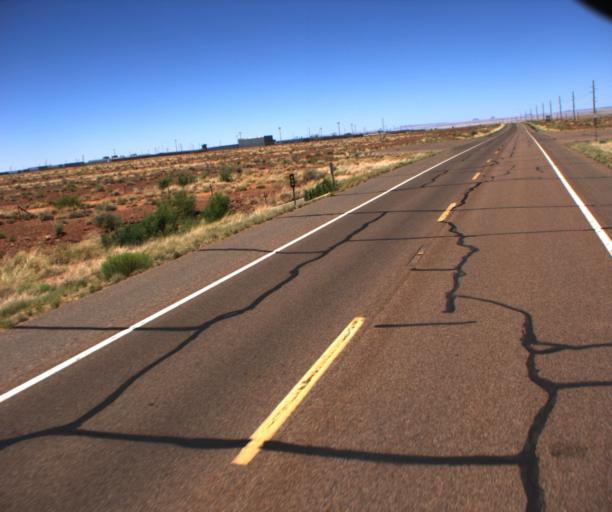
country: US
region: Arizona
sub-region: Navajo County
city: Winslow
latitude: 34.9765
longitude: -110.7227
